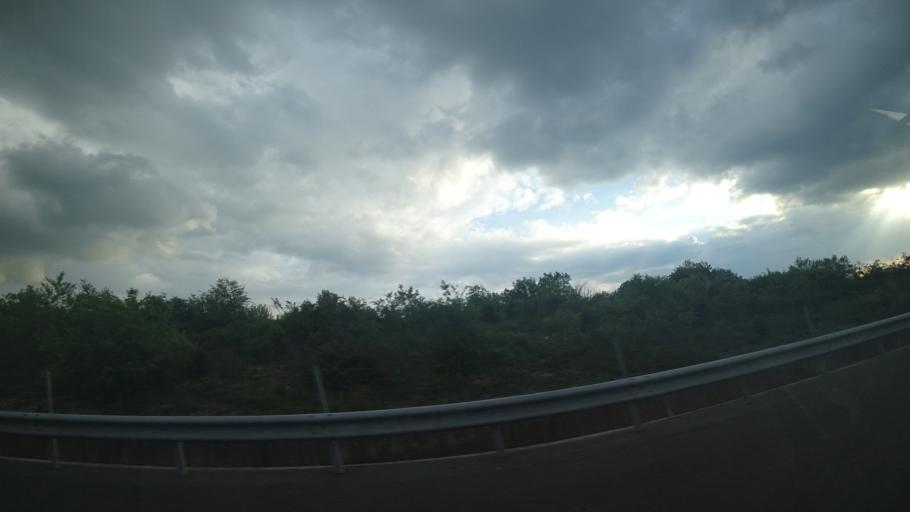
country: FR
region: Midi-Pyrenees
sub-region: Departement de l'Aveyron
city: La Cavalerie
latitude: 44.0174
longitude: 3.1324
